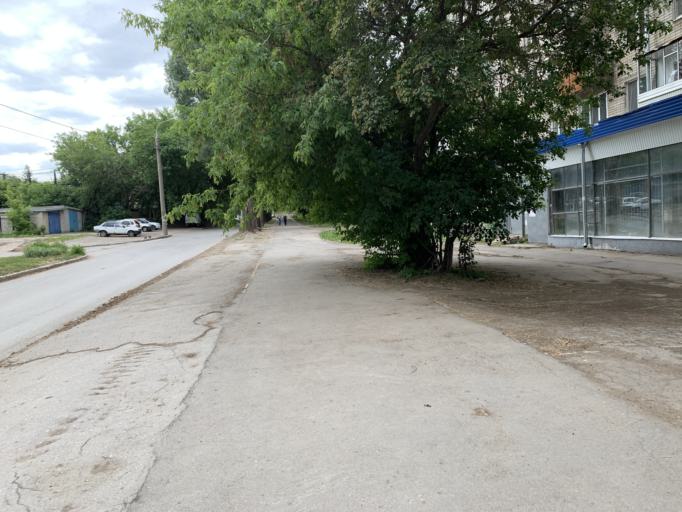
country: RU
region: Samara
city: Samara
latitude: 53.2144
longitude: 50.1720
